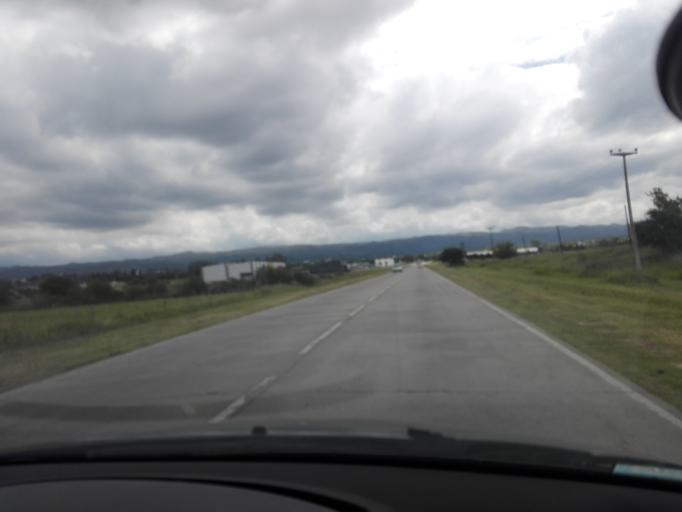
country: AR
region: Cordoba
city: Alta Gracia
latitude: -31.6347
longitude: -64.4265
